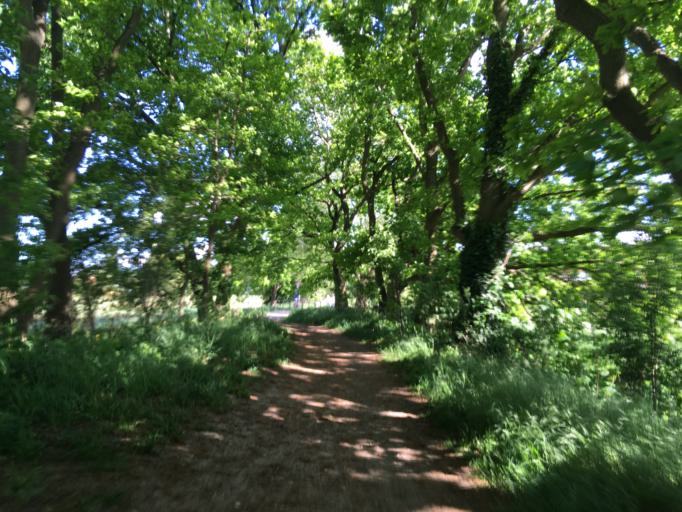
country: DE
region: Berlin
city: Buch
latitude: 52.6443
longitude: 13.5101
